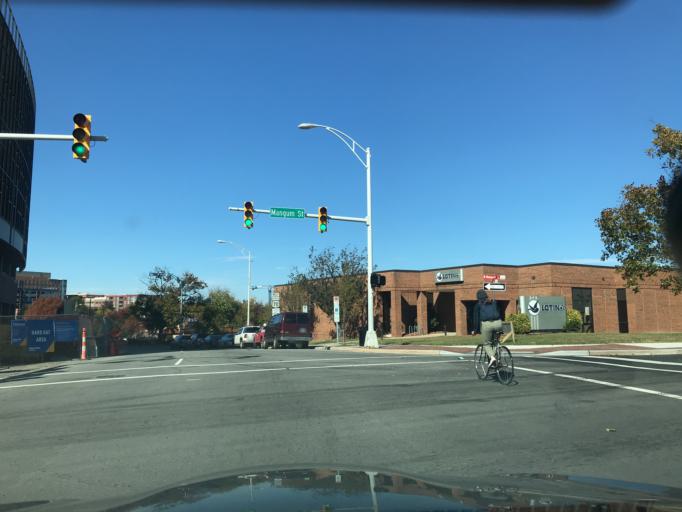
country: US
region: North Carolina
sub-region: Durham County
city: Durham
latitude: 35.9975
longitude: -78.8984
